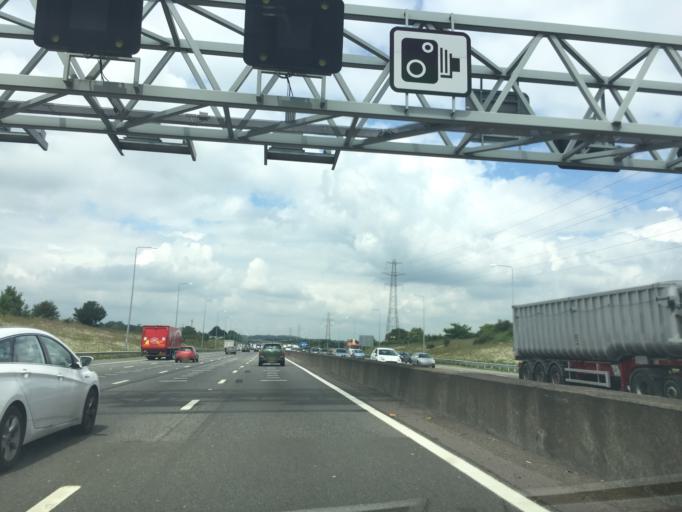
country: GB
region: England
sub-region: Buckinghamshire
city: Chalfont Saint Peter
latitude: 51.6052
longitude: -0.5290
